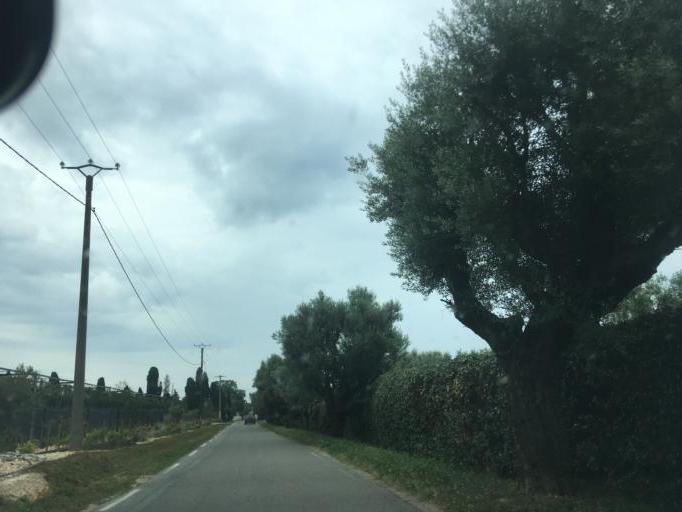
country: FR
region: Provence-Alpes-Cote d'Azur
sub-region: Departement du Var
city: La Londe-les-Maures
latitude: 43.1467
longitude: 6.2287
